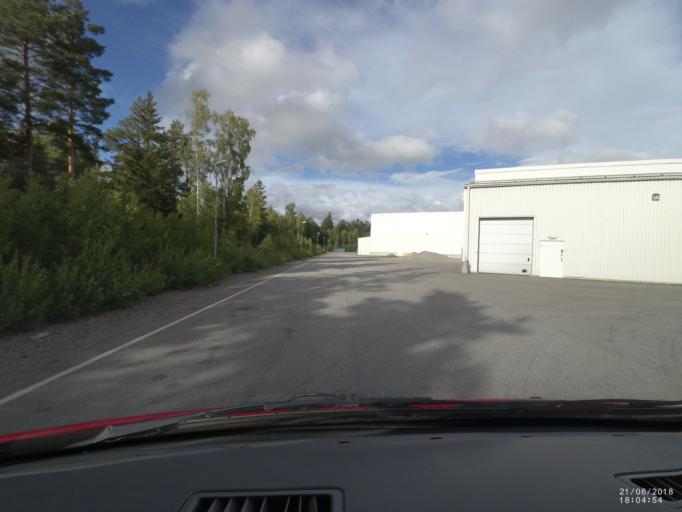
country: SE
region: Soedermanland
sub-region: Nykopings Kommun
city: Nykoping
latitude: 58.7721
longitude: 17.0146
